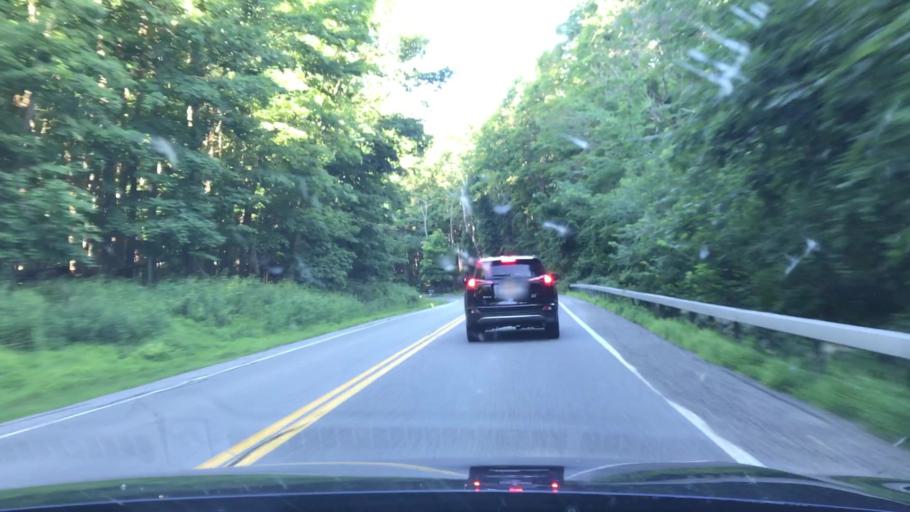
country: US
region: New York
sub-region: Putnam County
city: Mahopac
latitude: 41.3734
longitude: -73.6997
